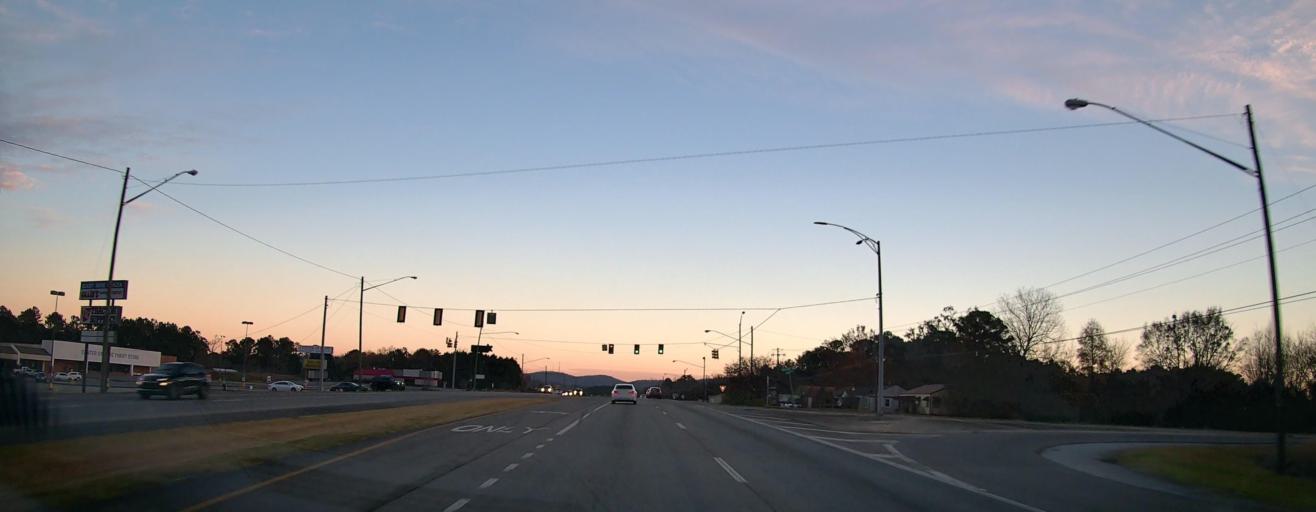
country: US
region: Alabama
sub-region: Etowah County
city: Glencoe
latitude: 33.9743
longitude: -85.9516
